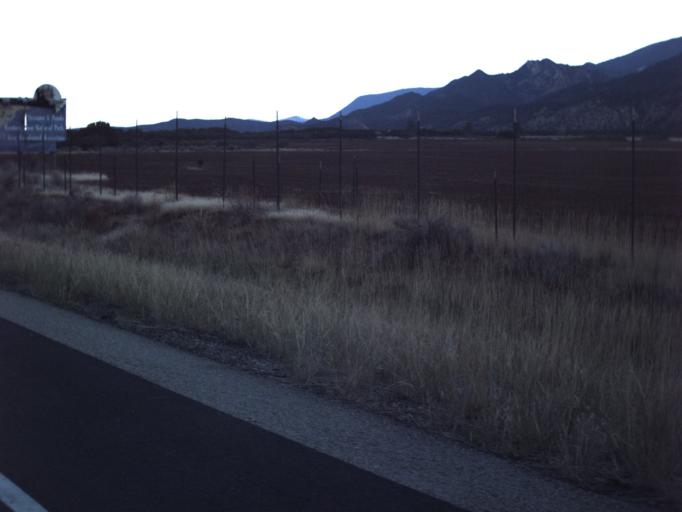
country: US
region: Utah
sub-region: Iron County
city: Cedar City
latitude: 37.5095
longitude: -113.2130
